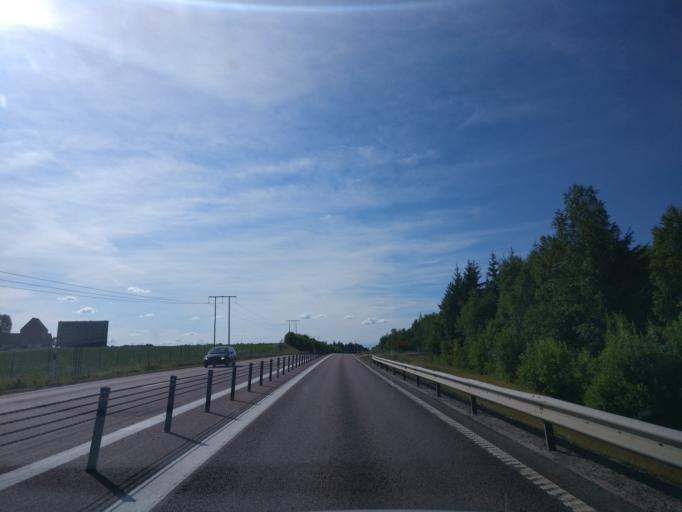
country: SE
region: Vaermland
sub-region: Kils Kommun
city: Kil
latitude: 59.4997
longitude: 13.2718
